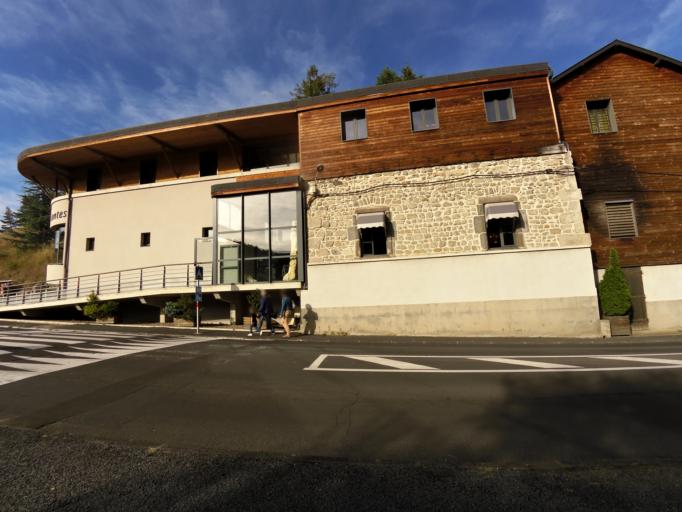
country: FR
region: Auvergne
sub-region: Departement du Puy-de-Dome
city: Aydat
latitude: 45.5828
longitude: 2.9924
